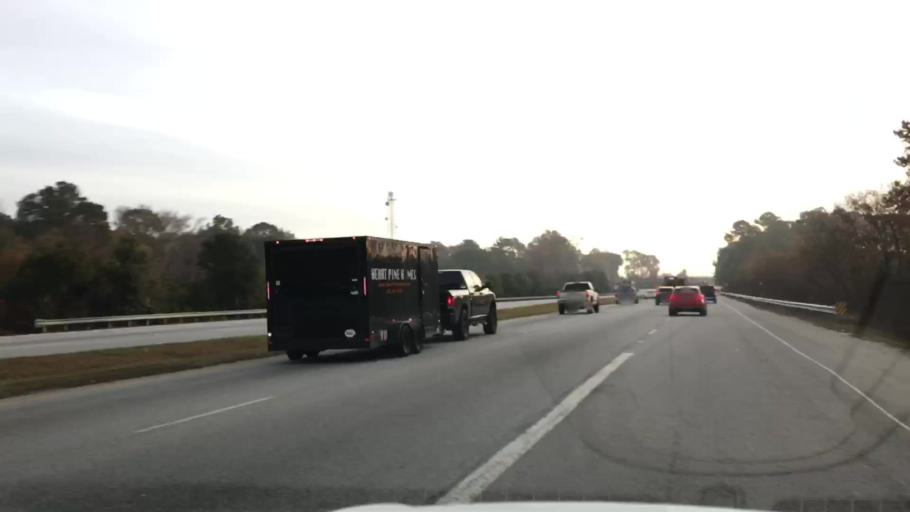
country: US
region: South Carolina
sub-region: Charleston County
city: Shell Point
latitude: 32.8122
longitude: -80.0527
